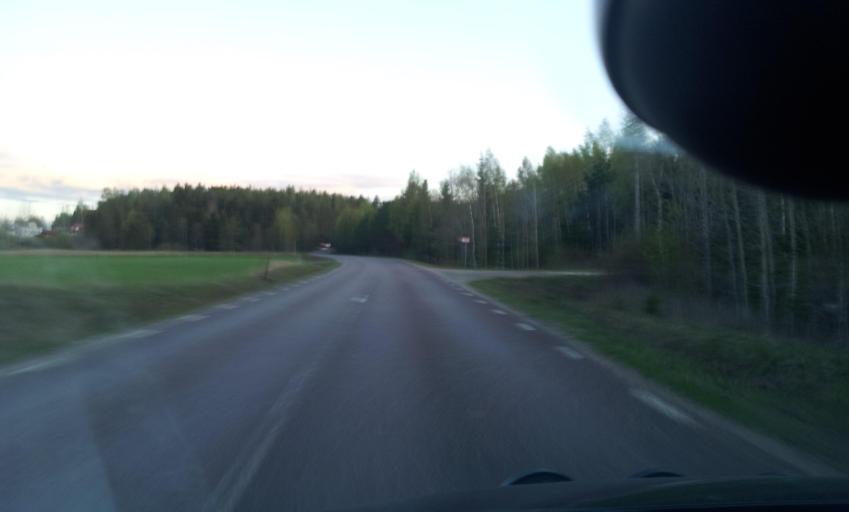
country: SE
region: Gaevleborg
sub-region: Bollnas Kommun
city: Bollnas
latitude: 61.3799
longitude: 16.4031
